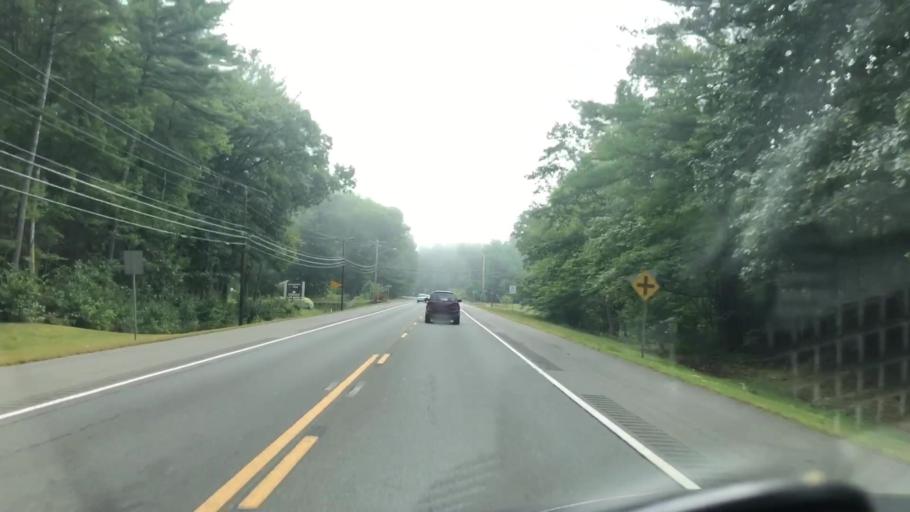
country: US
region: Massachusetts
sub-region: Franklin County
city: Bernardston
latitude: 42.6695
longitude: -72.5245
